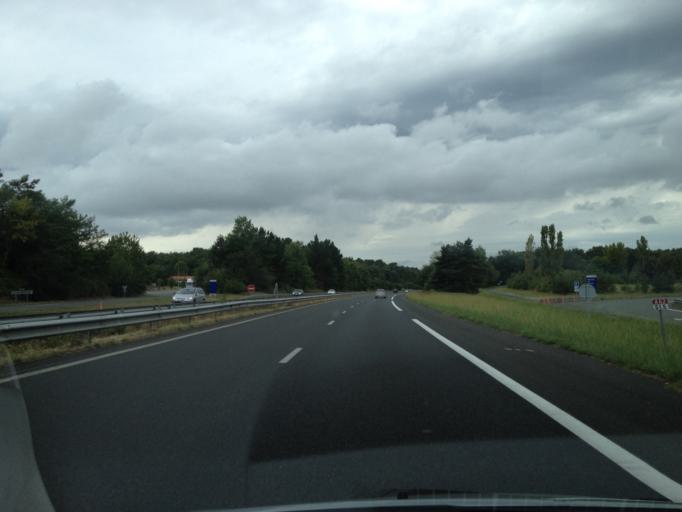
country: FR
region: Aquitaine
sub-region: Departement de la Gironde
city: Gironde-sur-Dropt
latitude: 44.5167
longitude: -0.0782
